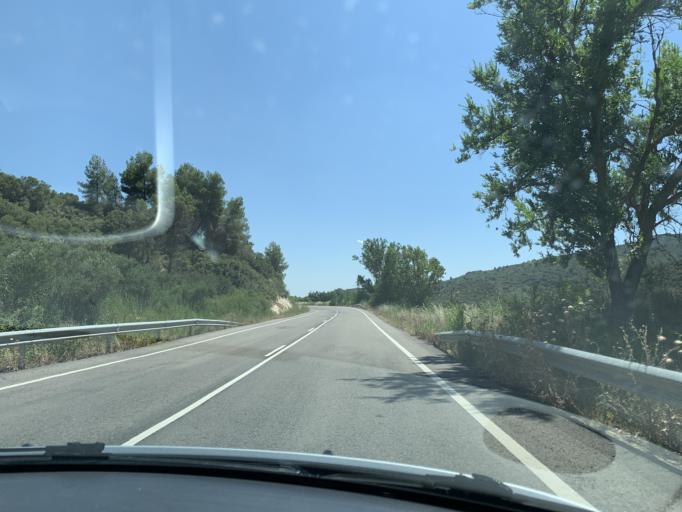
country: ES
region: Castille-La Mancha
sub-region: Provincia de Guadalajara
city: Pastrana
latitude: 40.3769
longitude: -2.9108
